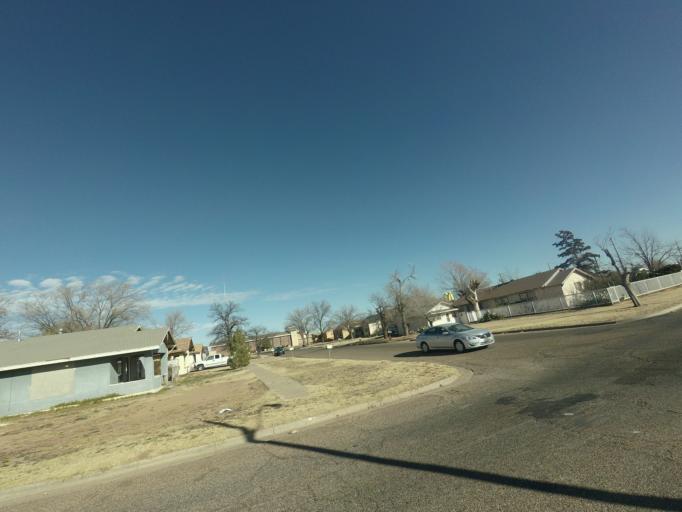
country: US
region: New Mexico
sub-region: Curry County
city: Clovis
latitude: 34.4109
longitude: -103.2081
